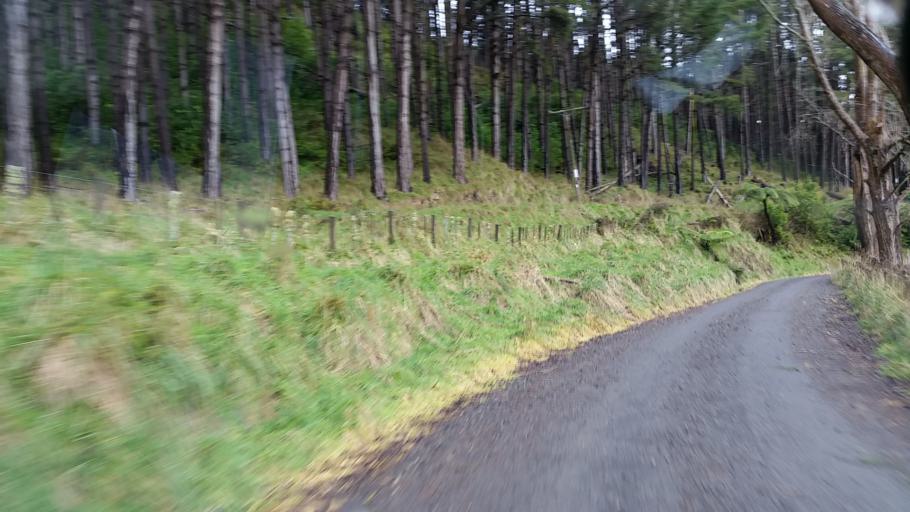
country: NZ
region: Taranaki
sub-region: South Taranaki District
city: Eltham
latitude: -39.5029
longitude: 174.4084
